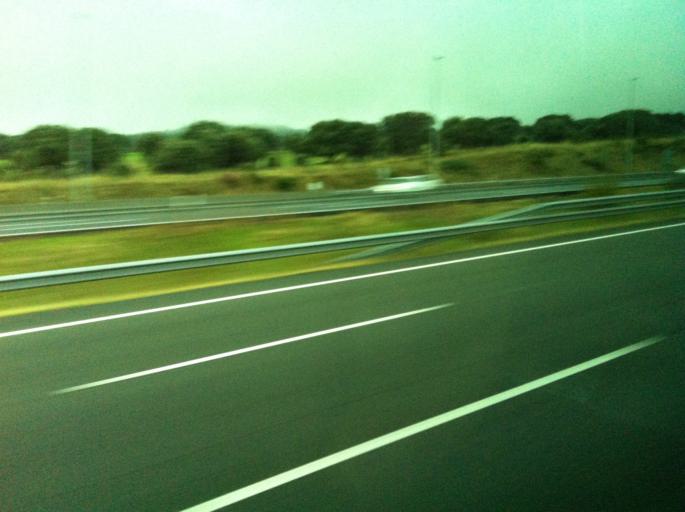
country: ES
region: Madrid
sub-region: Provincia de Madrid
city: Guadarrama
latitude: 40.6631
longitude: -4.0995
